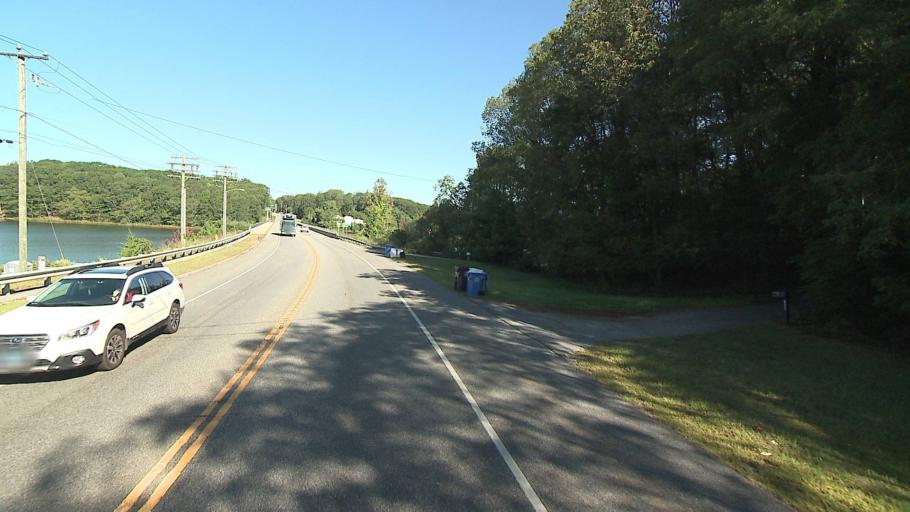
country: US
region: Connecticut
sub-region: New London County
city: Gales Ferry
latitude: 41.4703
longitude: -72.0590
